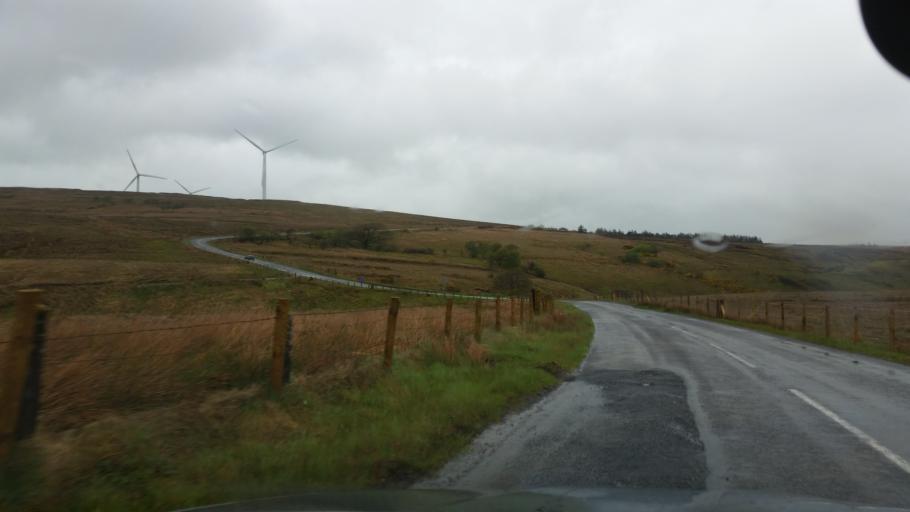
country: GB
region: Northern Ireland
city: Fintona
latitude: 54.4426
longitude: -7.3243
